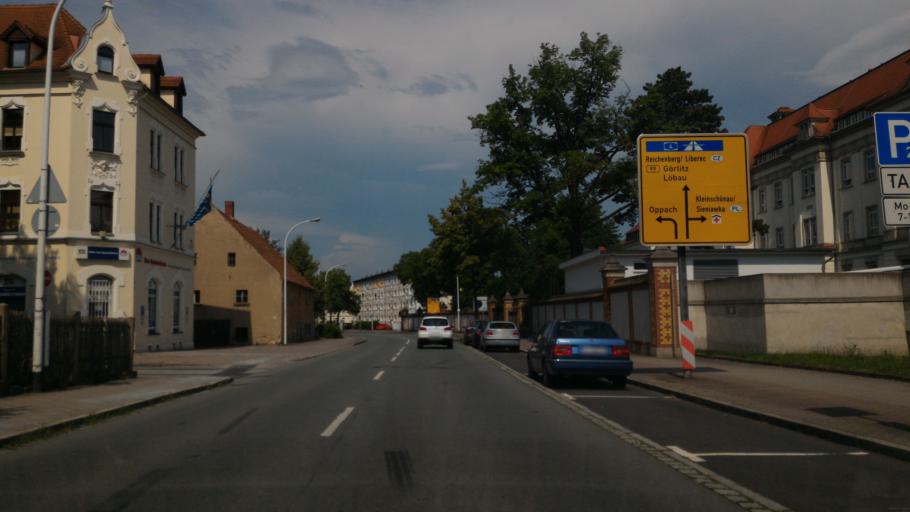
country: DE
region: Saxony
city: Zittau
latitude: 50.8995
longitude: 14.8198
